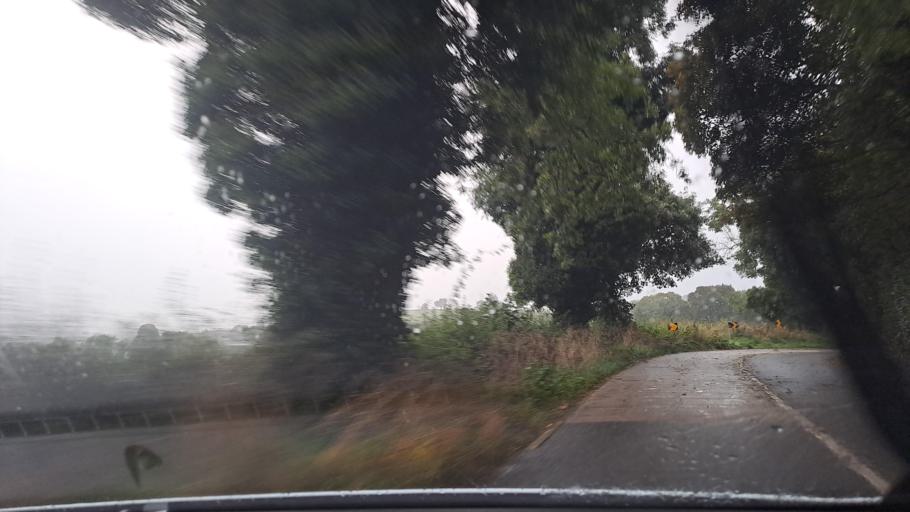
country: IE
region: Ulster
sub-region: County Monaghan
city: Carrickmacross
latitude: 53.9858
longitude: -6.7015
